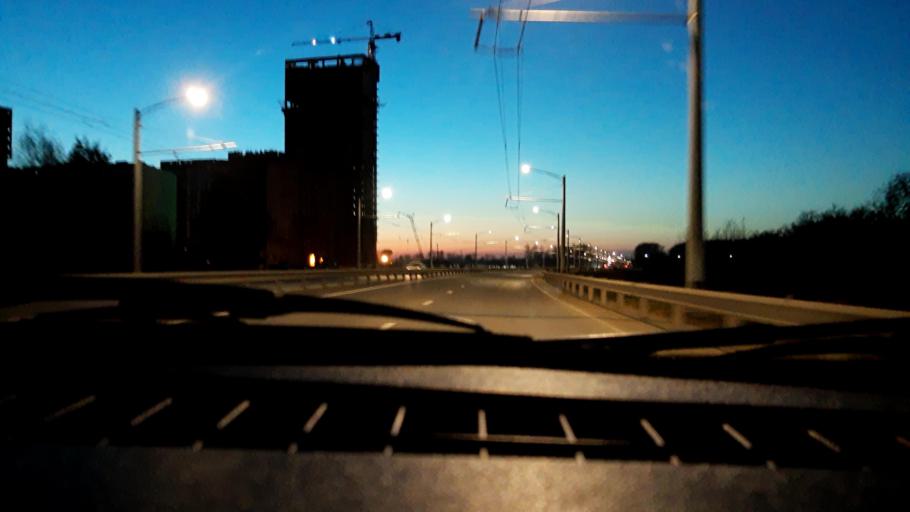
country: RU
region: Bashkortostan
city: Mikhaylovka
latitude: 54.7707
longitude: 55.9063
